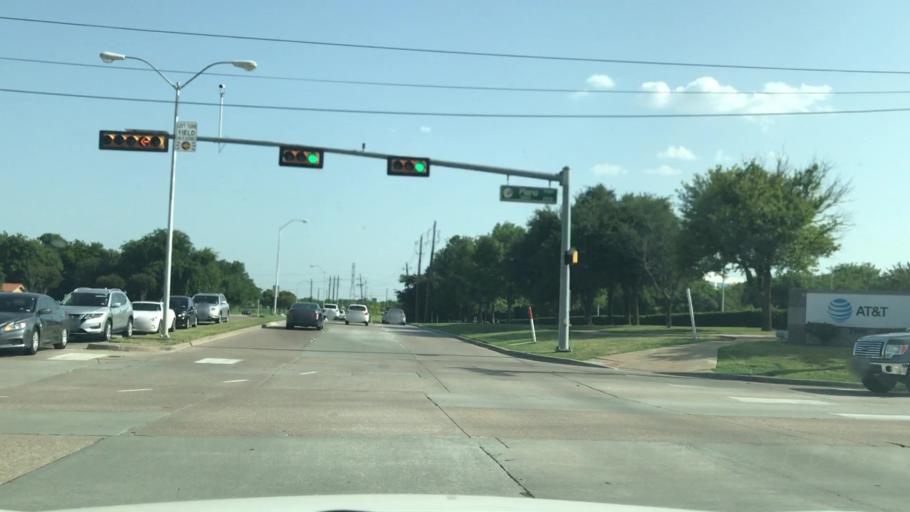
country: US
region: Texas
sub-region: Collin County
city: Plano
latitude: 33.0086
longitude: -96.7502
